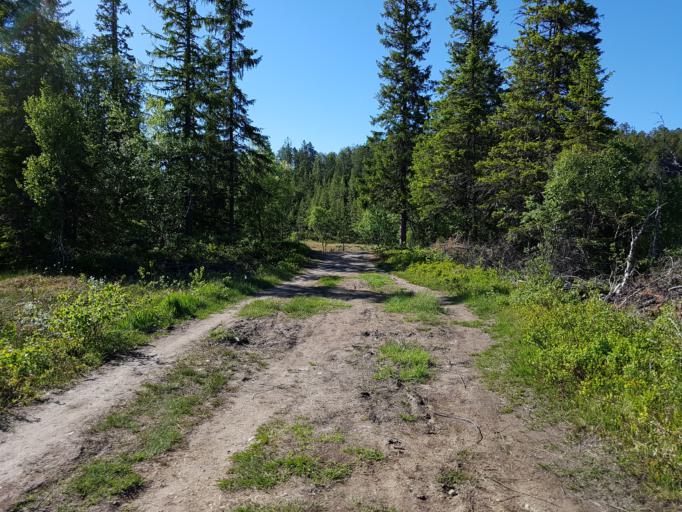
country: NO
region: Sor-Trondelag
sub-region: Trondheim
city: Trondheim
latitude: 63.4286
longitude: 10.2923
